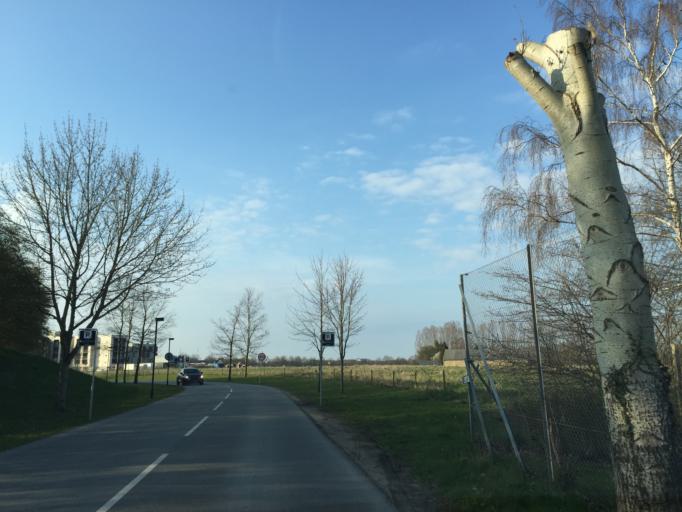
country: DK
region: South Denmark
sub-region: Odense Kommune
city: Neder Holluf
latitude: 55.3716
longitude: 10.4326
